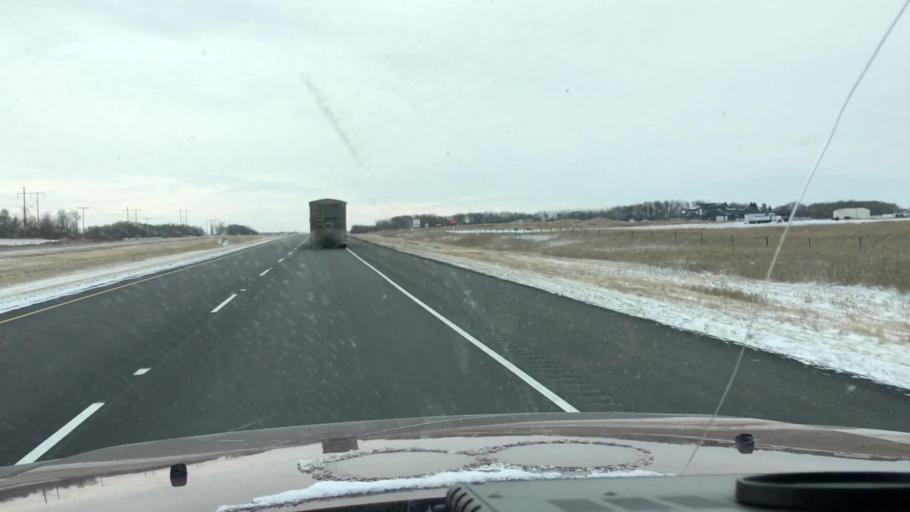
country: CA
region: Saskatchewan
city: Saskatoon
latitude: 51.9454
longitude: -106.5425
